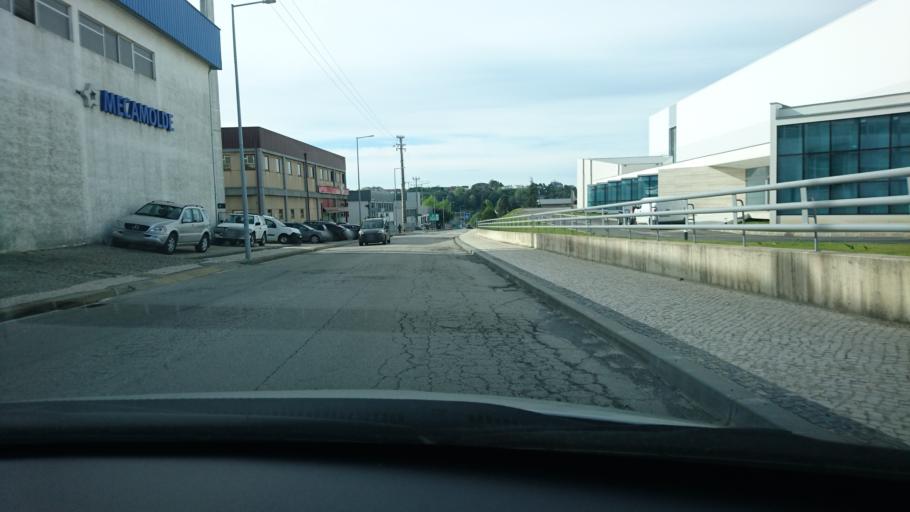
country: PT
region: Aveiro
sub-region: Oliveira de Azemeis
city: Oliveira de Azemeis
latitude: 40.8512
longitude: -8.4801
